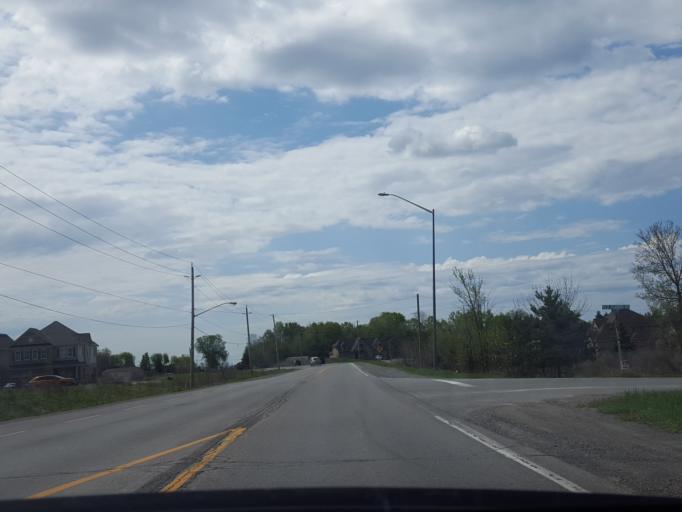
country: CA
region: Ontario
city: Oshawa
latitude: 43.9355
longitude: -78.7128
